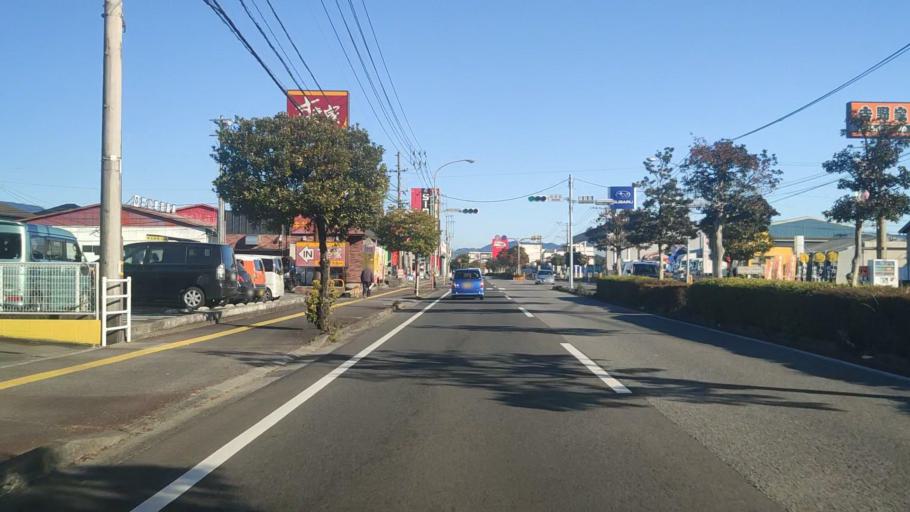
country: JP
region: Miyazaki
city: Nobeoka
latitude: 32.5657
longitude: 131.6825
